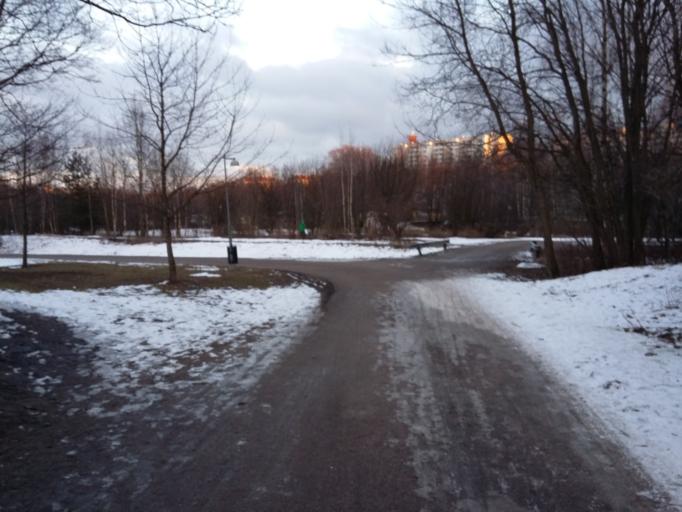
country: FI
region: Uusimaa
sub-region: Helsinki
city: Helsinki
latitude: 60.2010
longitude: 24.9527
